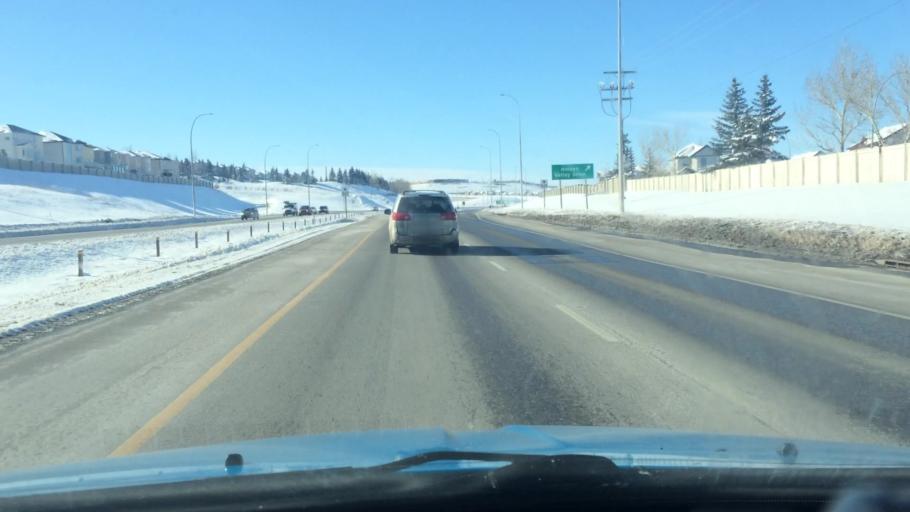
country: CA
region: Alberta
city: Calgary
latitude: 51.1461
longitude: -114.1313
